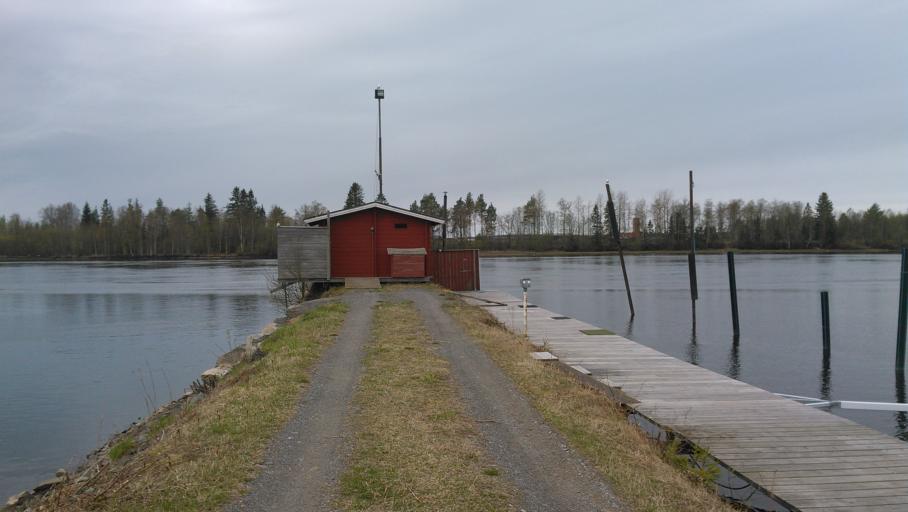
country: SE
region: Vaesterbotten
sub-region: Umea Kommun
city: Umea
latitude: 63.7884
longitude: 20.3085
